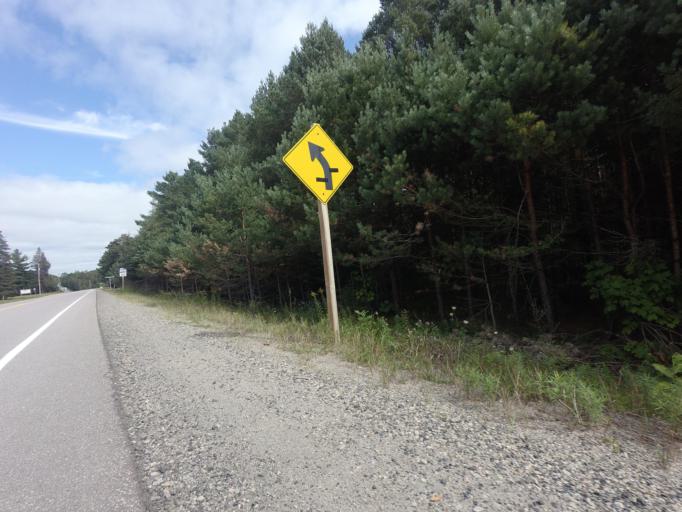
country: CA
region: Ontario
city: Bancroft
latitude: 44.9108
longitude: -78.3621
